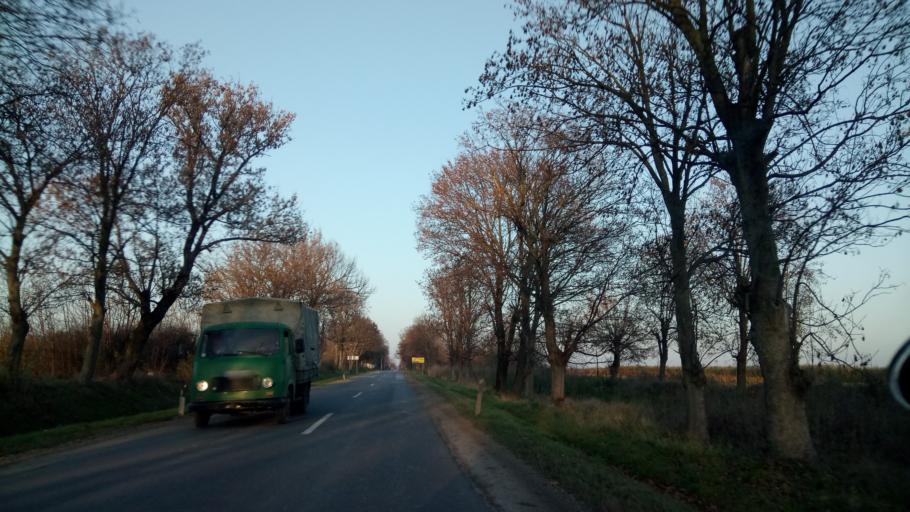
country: RS
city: Novi Slankamen
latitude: 45.1110
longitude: 20.2196
